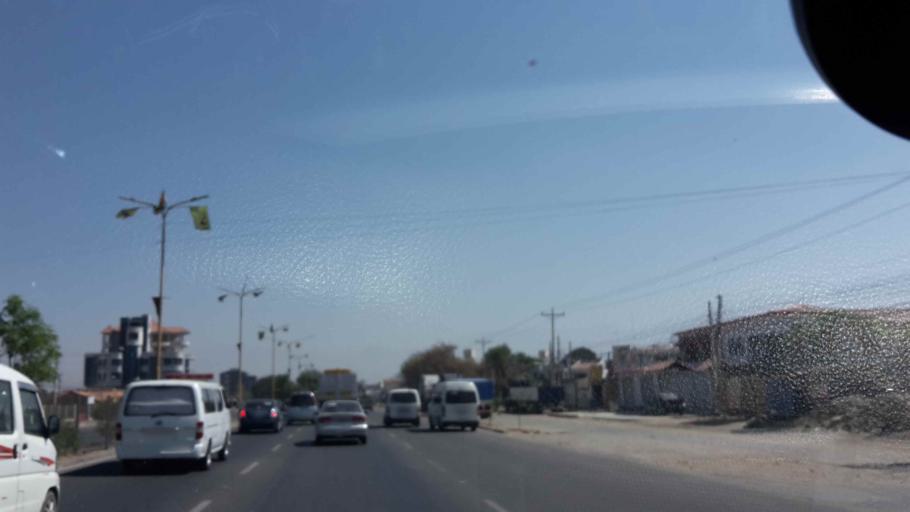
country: BO
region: Cochabamba
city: Cochabamba
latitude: -17.3916
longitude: -66.2220
